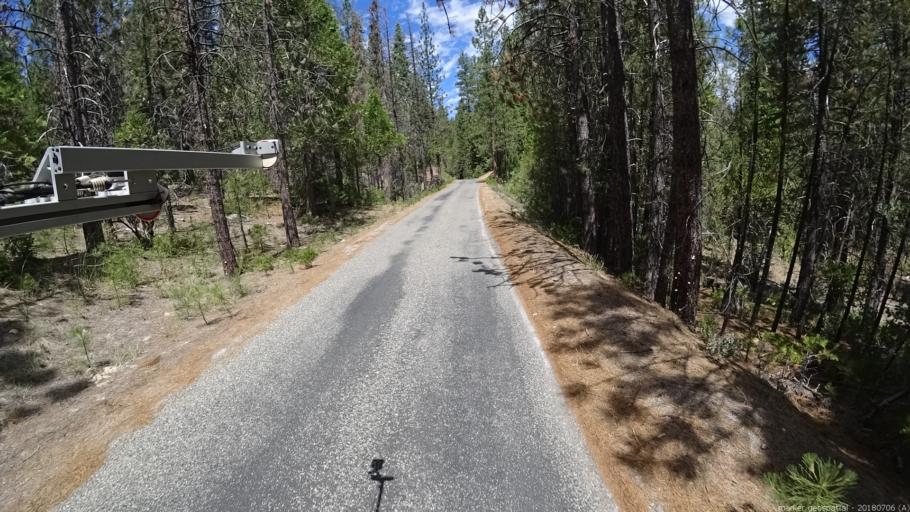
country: US
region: California
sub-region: Madera County
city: Oakhurst
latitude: 37.4052
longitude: -119.3950
